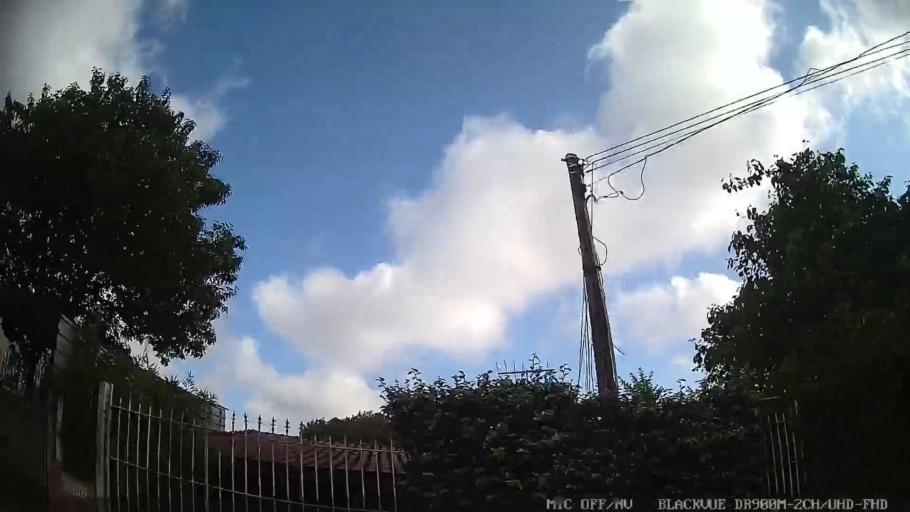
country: BR
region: Sao Paulo
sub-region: Sao Caetano Do Sul
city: Sao Caetano do Sul
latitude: -23.5768
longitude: -46.5233
